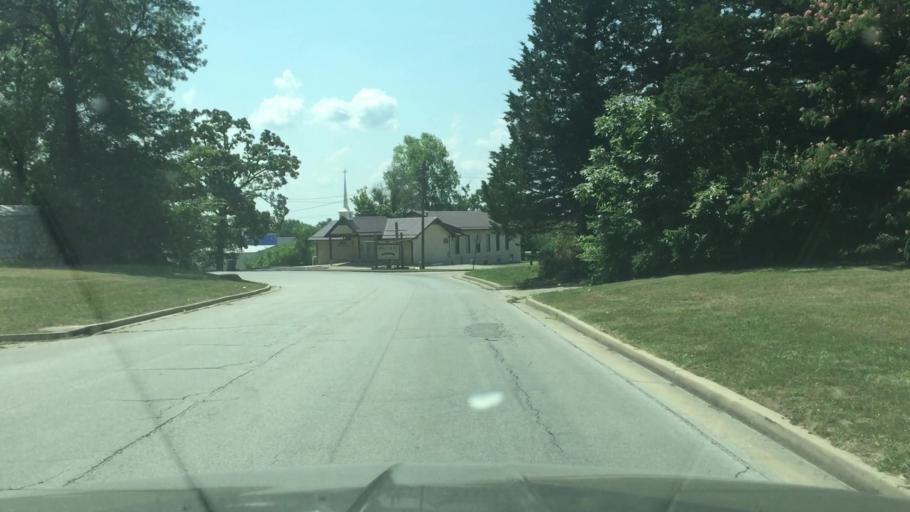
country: US
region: Missouri
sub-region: Miller County
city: Eldon
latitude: 38.3377
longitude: -92.5866
